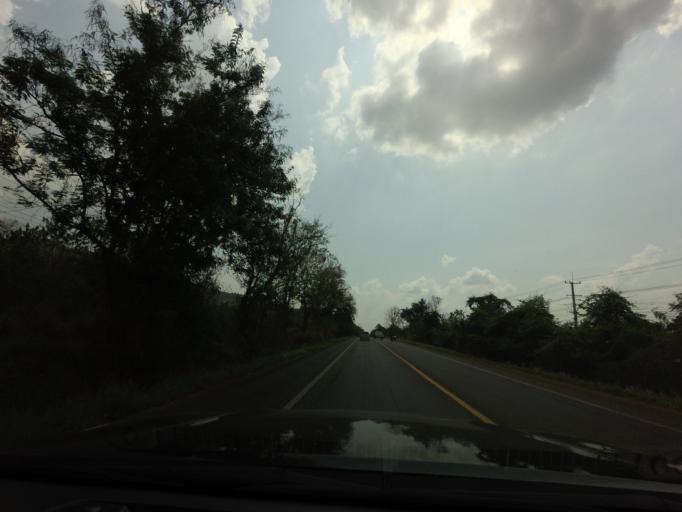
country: TH
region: Kanchanaburi
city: Sai Yok
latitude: 14.1555
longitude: 99.1401
